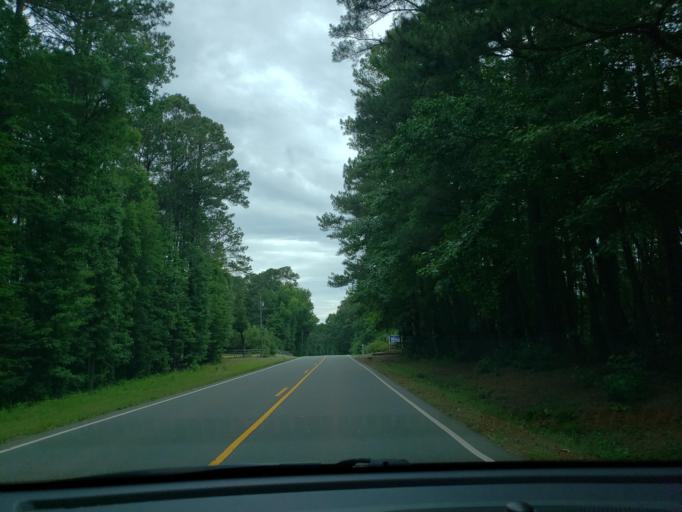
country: US
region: North Carolina
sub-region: Chatham County
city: Fearrington Village
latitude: 35.7739
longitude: -79.0044
